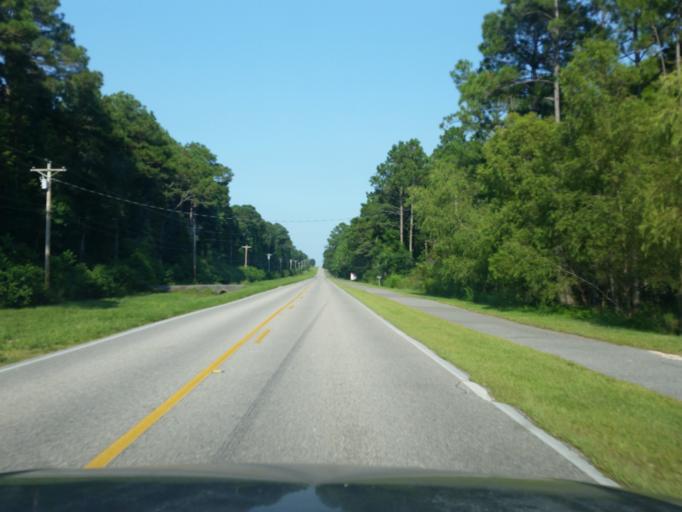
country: US
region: Alabama
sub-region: Baldwin County
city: Point Clear
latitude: 30.4211
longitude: -87.9041
